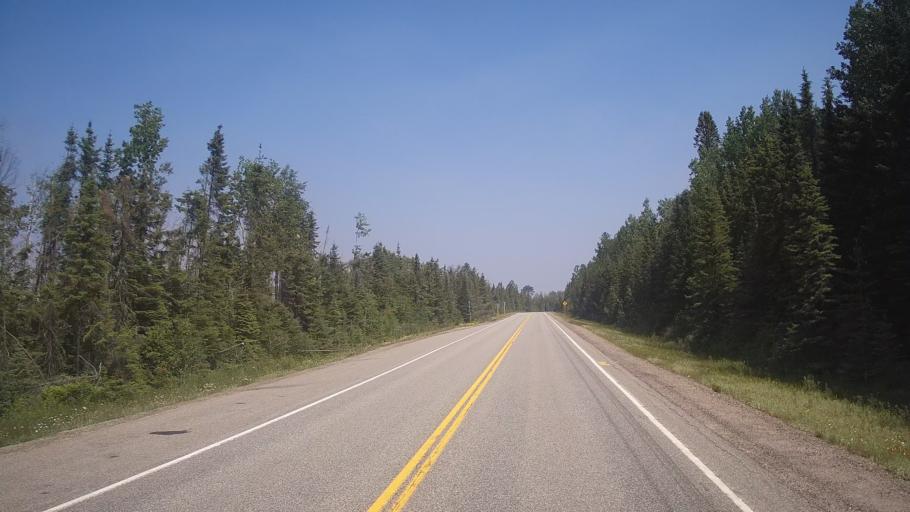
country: CA
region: Ontario
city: Timmins
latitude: 48.0486
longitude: -81.5835
